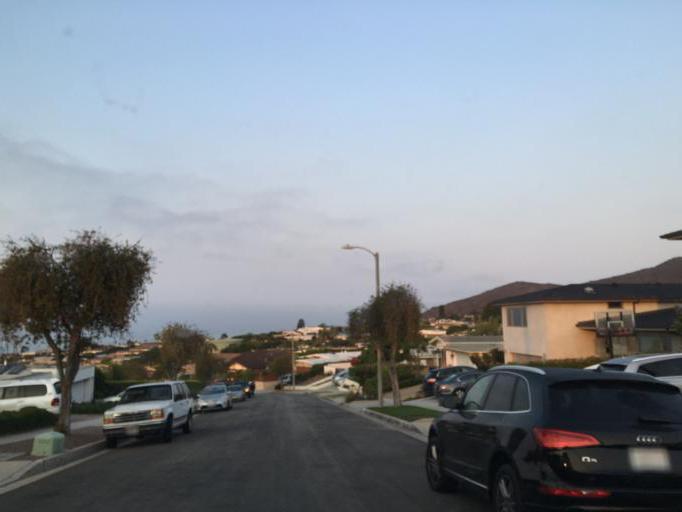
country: US
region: California
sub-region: Los Angeles County
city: Topanga
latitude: 34.0462
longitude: -118.5724
